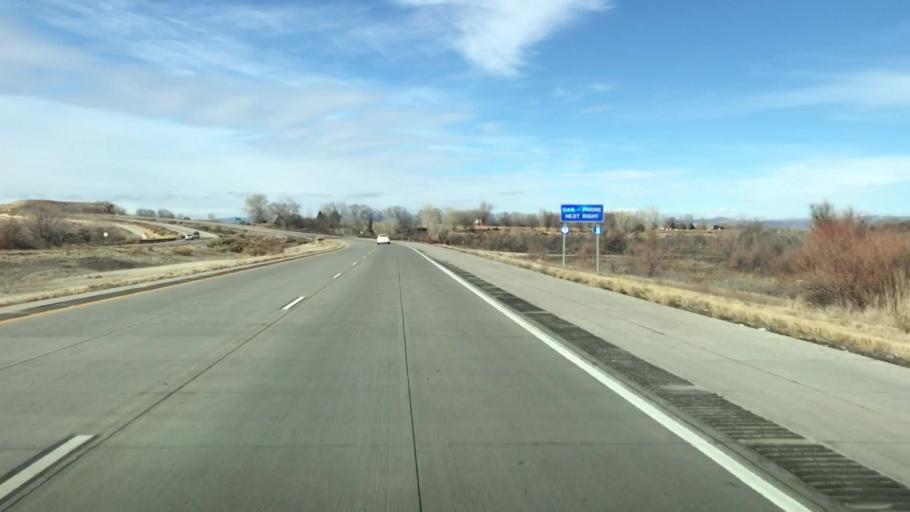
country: US
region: Colorado
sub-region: Mesa County
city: Loma
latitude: 39.1740
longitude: -108.7982
